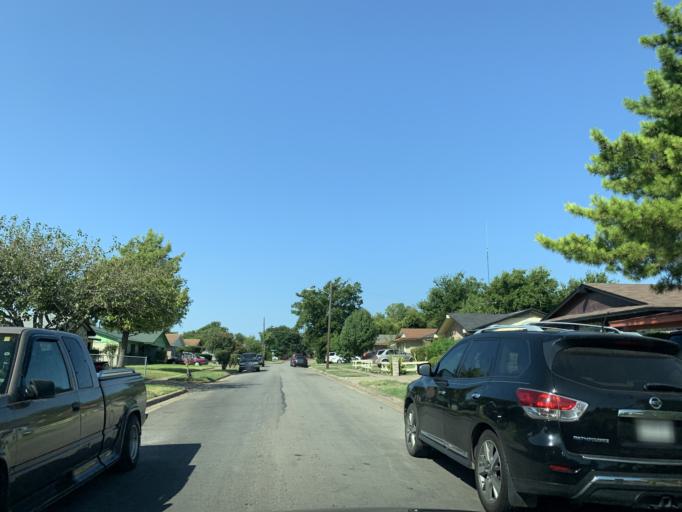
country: US
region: Texas
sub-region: Dallas County
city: Hutchins
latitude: 32.6668
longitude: -96.7619
